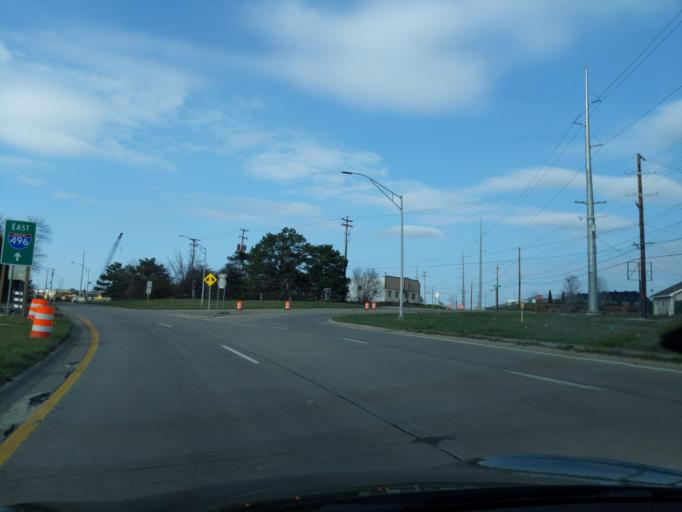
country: US
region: Michigan
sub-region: Ingham County
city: Edgemont Park
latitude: 42.7236
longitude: -84.5870
